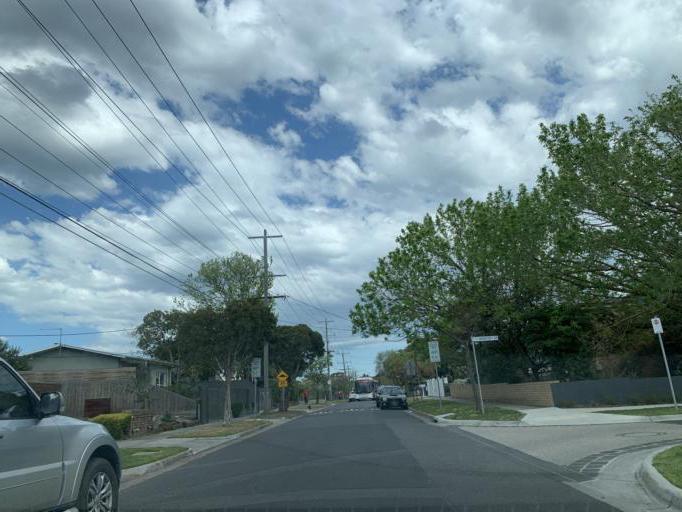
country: AU
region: Victoria
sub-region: Bayside
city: Highett
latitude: -37.9605
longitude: 145.0426
